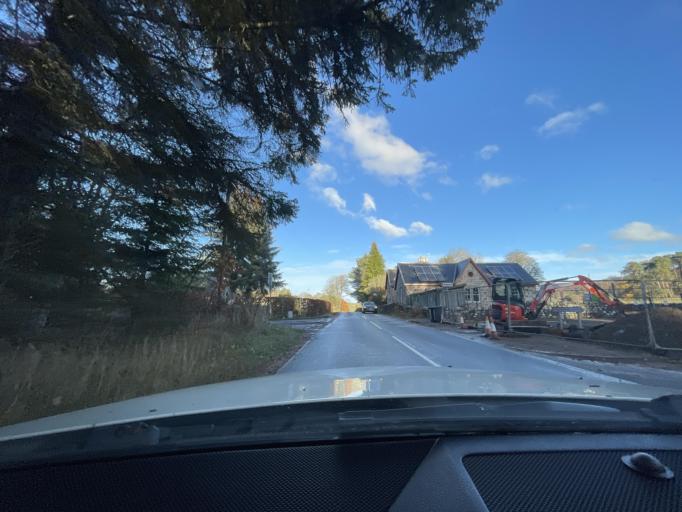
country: GB
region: Scotland
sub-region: Highland
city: Inverness
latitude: 57.3959
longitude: -4.3205
